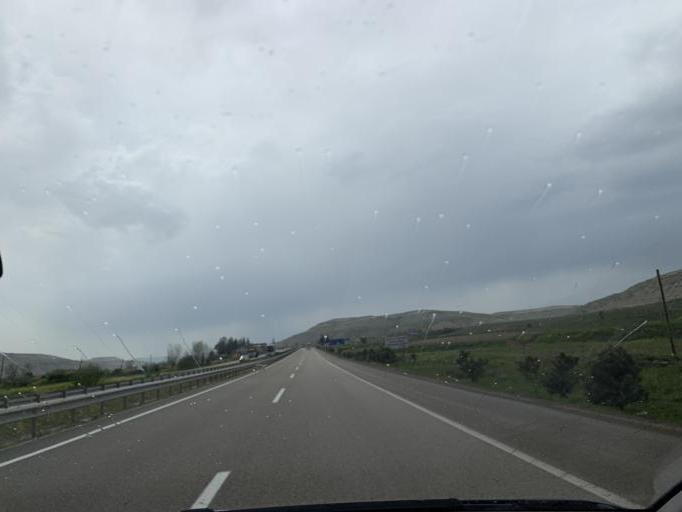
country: TR
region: Eskisehir
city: Gunyuzu
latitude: 39.5506
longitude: 31.7427
